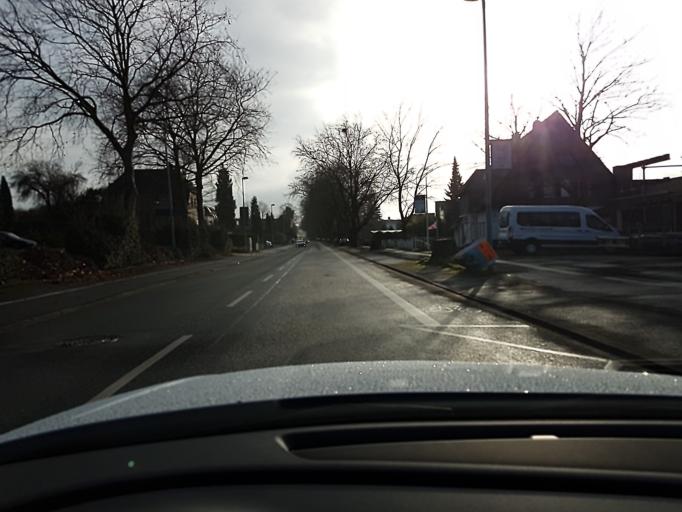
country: DE
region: North Rhine-Westphalia
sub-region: Regierungsbezirk Dusseldorf
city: Muelheim (Ruhr)
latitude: 51.4083
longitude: 6.8948
